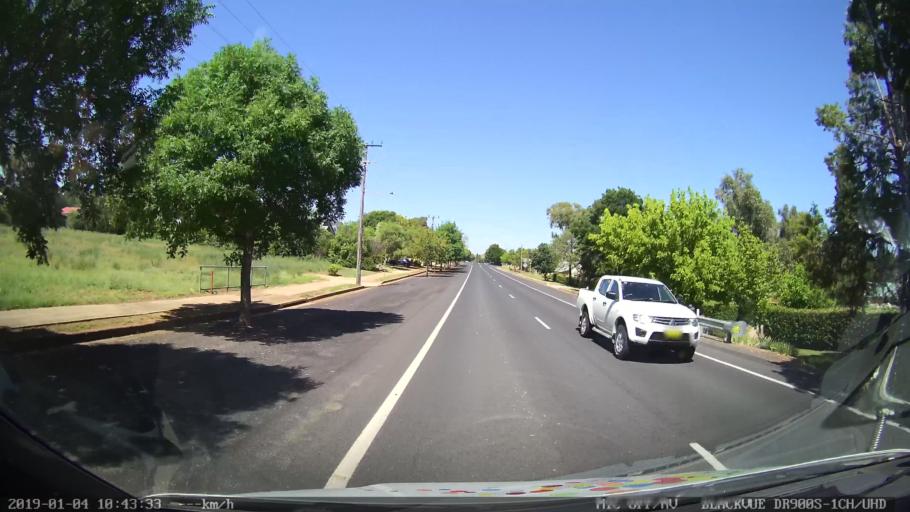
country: AU
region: New South Wales
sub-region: Cabonne
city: Molong
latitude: -33.2850
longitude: 148.7432
